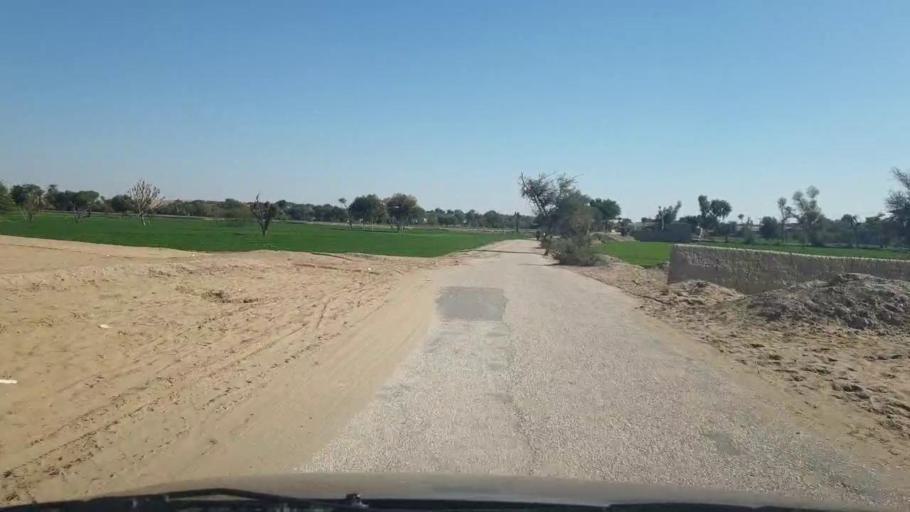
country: PK
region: Sindh
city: Bozdar
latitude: 27.0603
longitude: 68.6315
